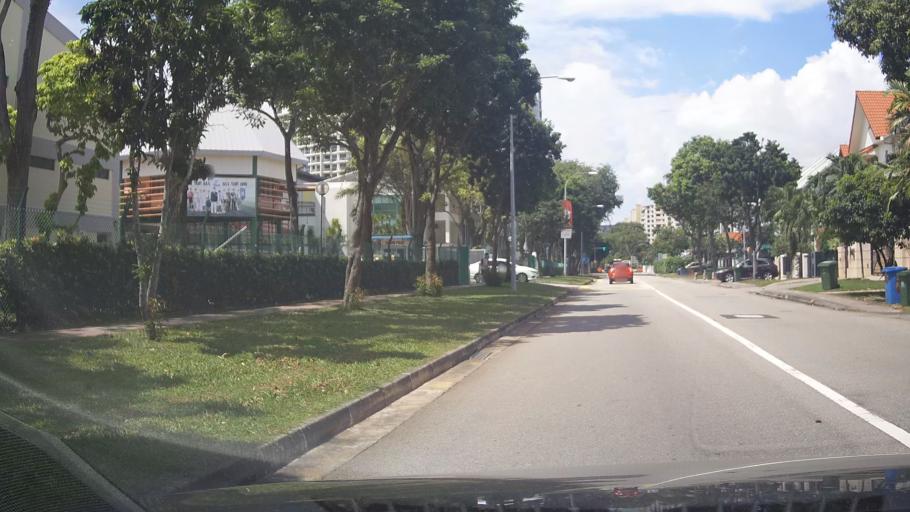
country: SG
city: Singapore
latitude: 1.3080
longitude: 103.8983
